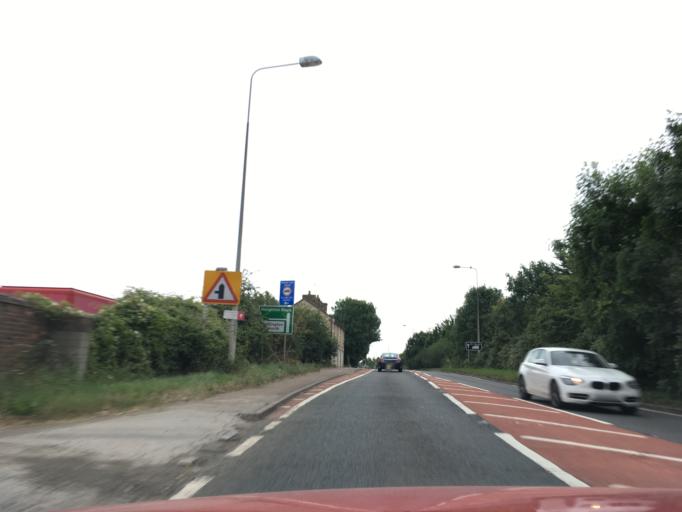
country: GB
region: England
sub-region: Central Bedfordshire
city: Hockliffe
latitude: 51.9250
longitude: -0.5771
